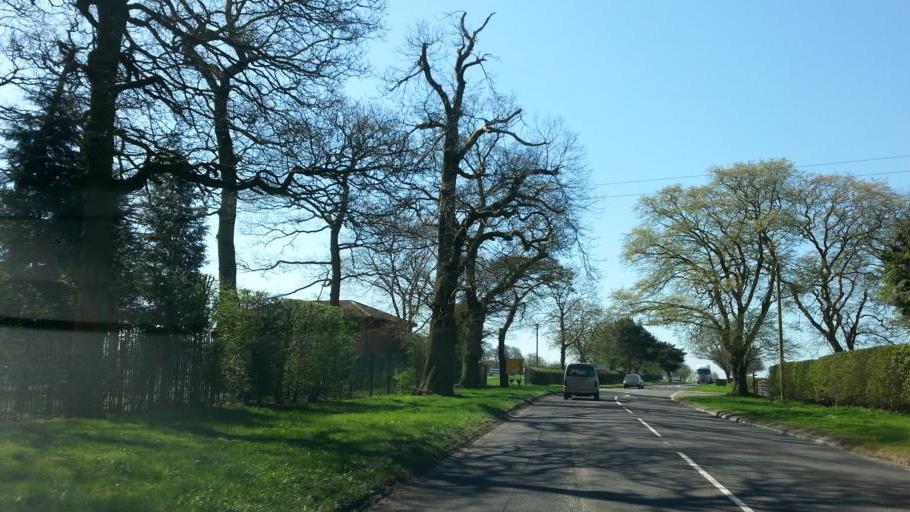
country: GB
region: England
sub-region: Staffordshire
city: Stafford
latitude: 52.8282
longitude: -2.0659
